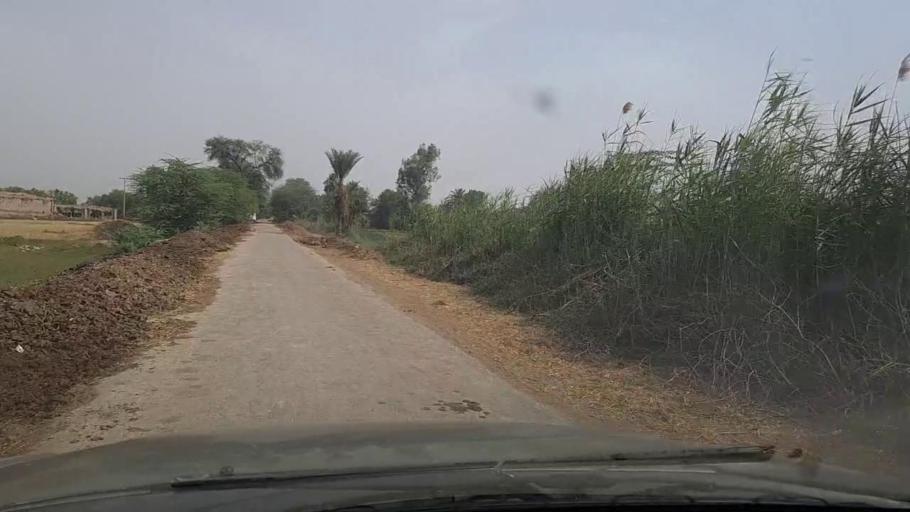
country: PK
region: Sindh
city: Lakhi
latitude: 27.8430
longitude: 68.7601
